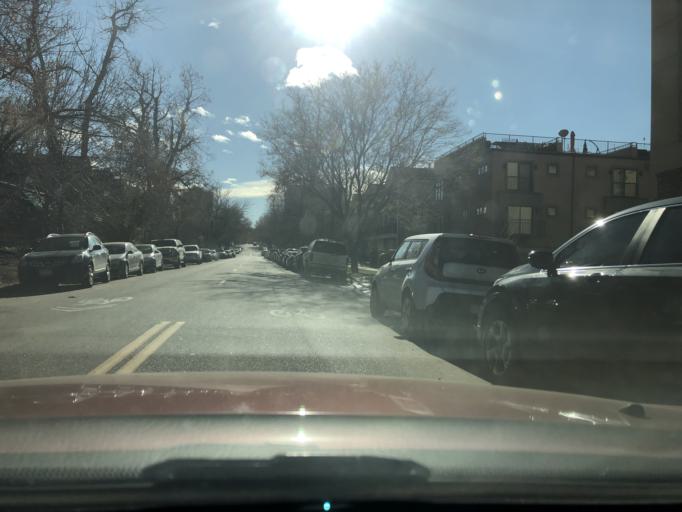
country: US
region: Colorado
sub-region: Denver County
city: Denver
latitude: 39.7431
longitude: -104.9685
